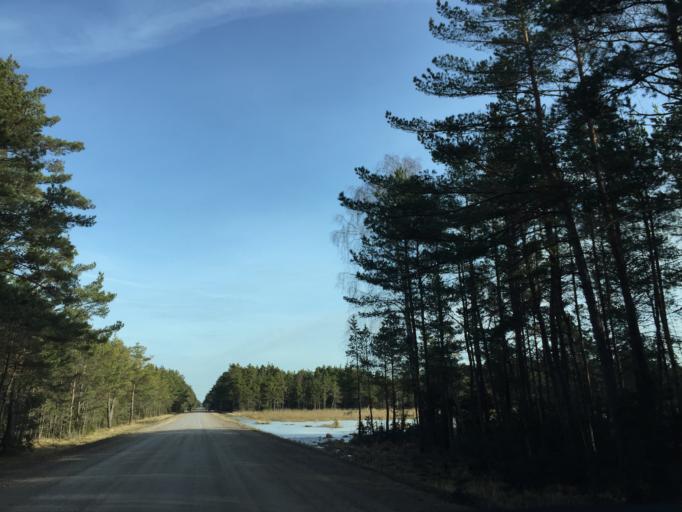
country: EE
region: Saare
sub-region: Kuressaare linn
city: Kuressaare
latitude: 58.3001
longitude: 21.9567
